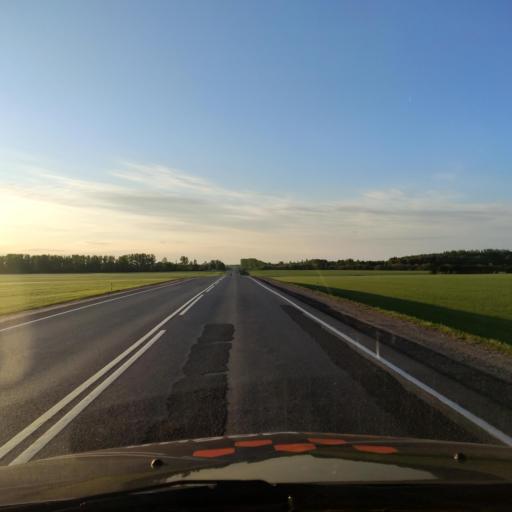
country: RU
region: Orjol
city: Livny
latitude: 52.4466
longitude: 37.5226
